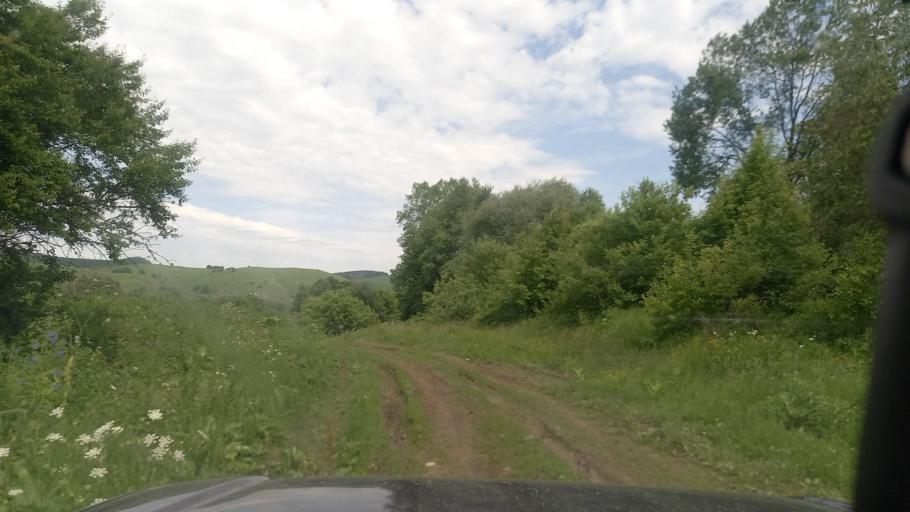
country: RU
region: Karachayevo-Cherkesiya
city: Pregradnaya
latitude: 44.0772
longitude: 41.2617
